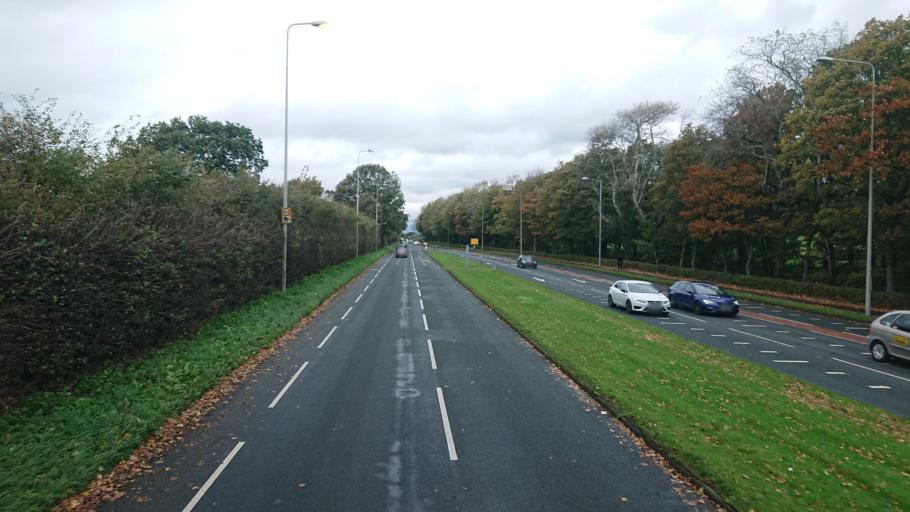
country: GB
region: England
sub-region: Lancashire
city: Galgate
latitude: 54.0116
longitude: -2.7946
